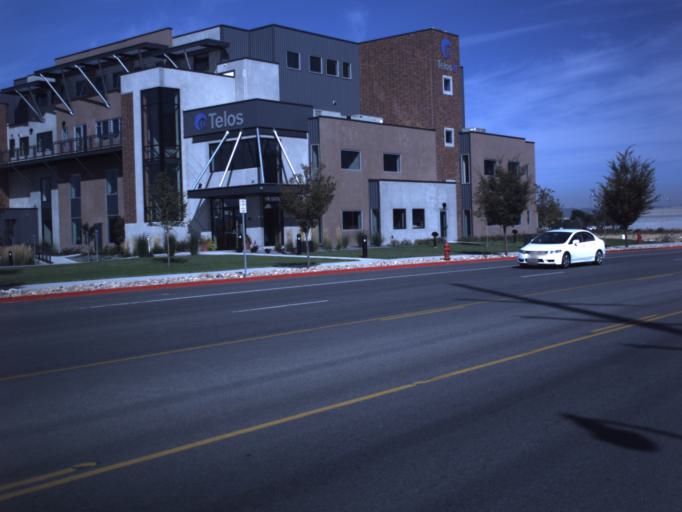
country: US
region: Utah
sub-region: Utah County
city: Orem
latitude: 40.2855
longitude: -111.7337
